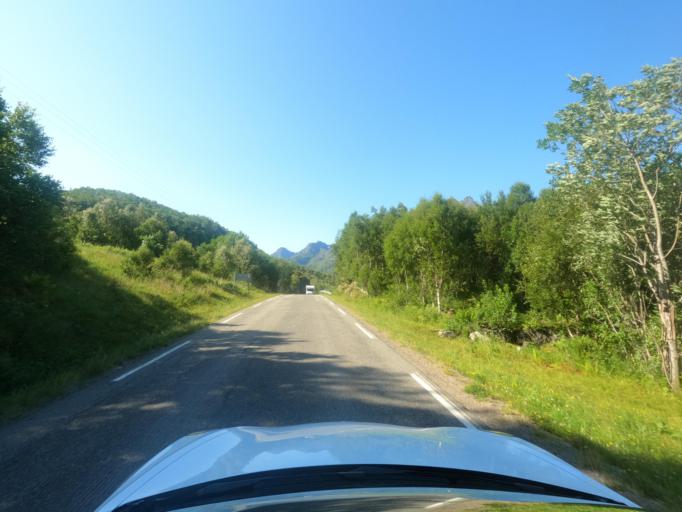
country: NO
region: Nordland
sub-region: Hadsel
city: Stokmarknes
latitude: 68.4344
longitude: 15.1776
